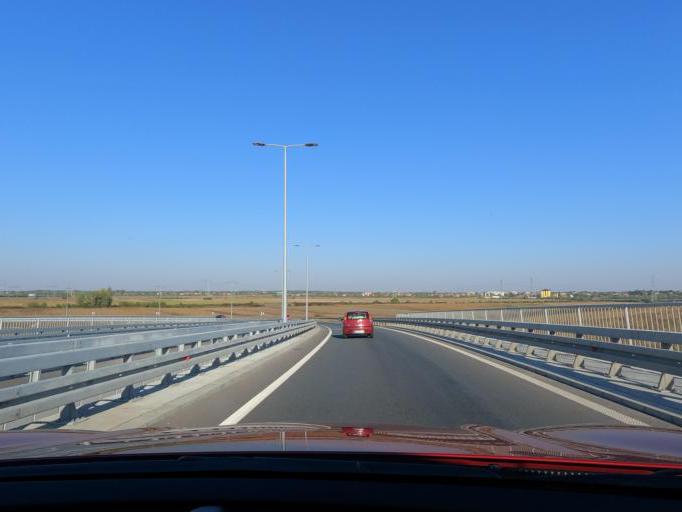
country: RS
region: Central Serbia
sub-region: Belgrade
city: Surcin
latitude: 44.7759
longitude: 20.2799
